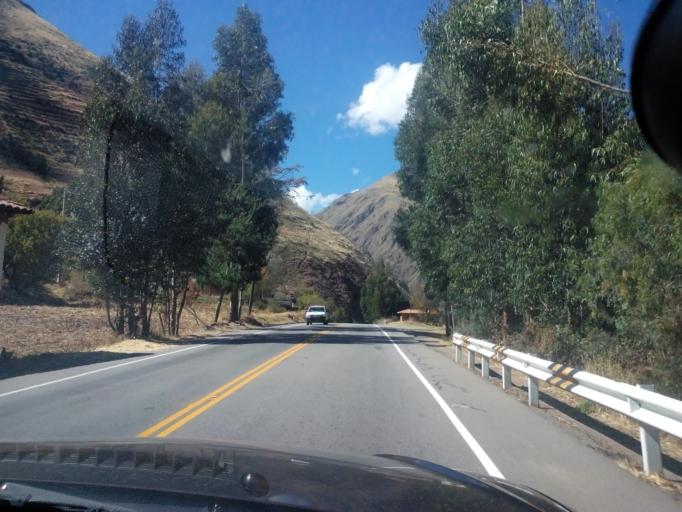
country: PE
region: Cusco
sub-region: Provincia de Quispicanchis
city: Quiquijana
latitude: -13.8034
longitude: -71.5471
